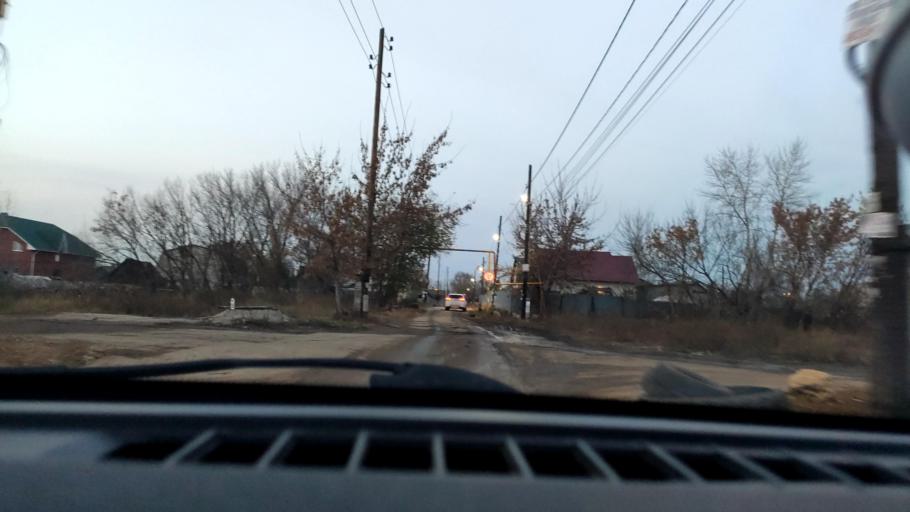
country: RU
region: Samara
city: Samara
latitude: 53.1398
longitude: 50.0964
